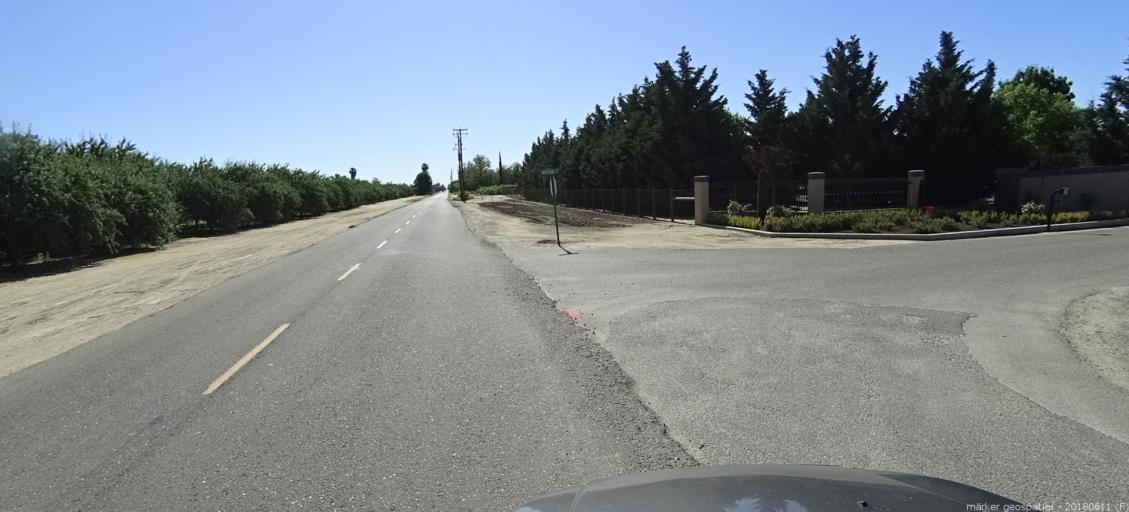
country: US
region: California
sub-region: Madera County
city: Madera
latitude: 36.9456
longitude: -120.1070
